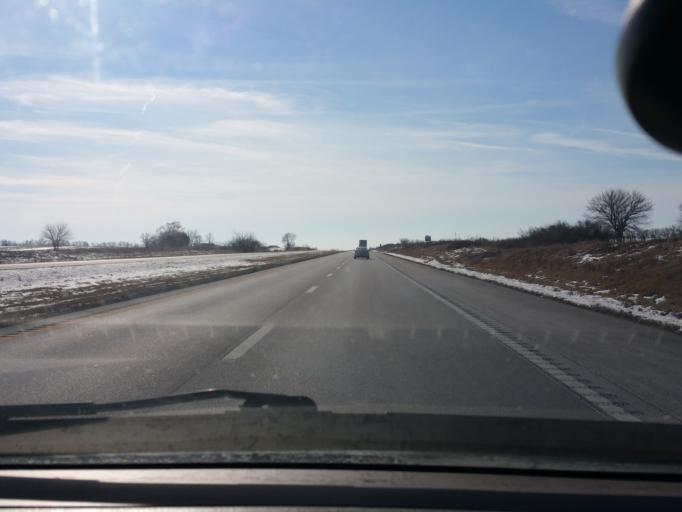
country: US
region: Missouri
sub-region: Clinton County
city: Cameron
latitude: 39.8024
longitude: -94.1997
